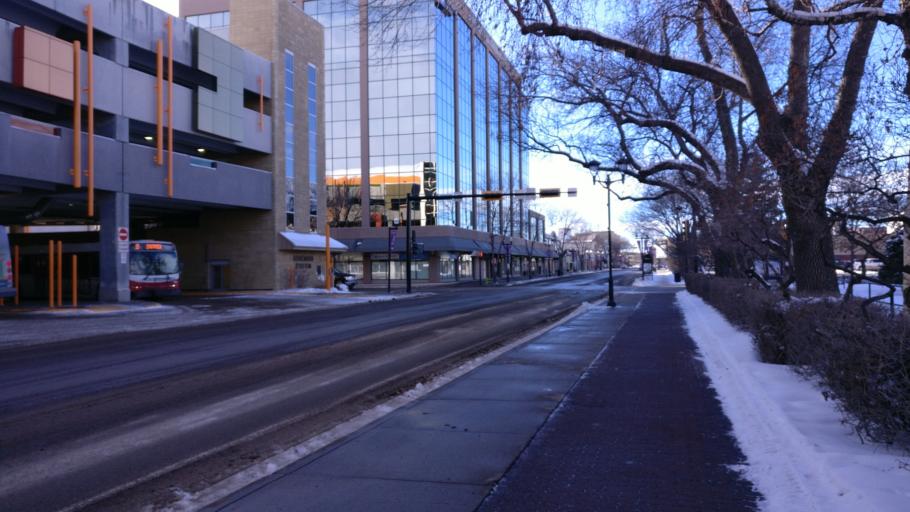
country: CA
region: Alberta
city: Red Deer
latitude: 52.2682
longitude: -113.8107
